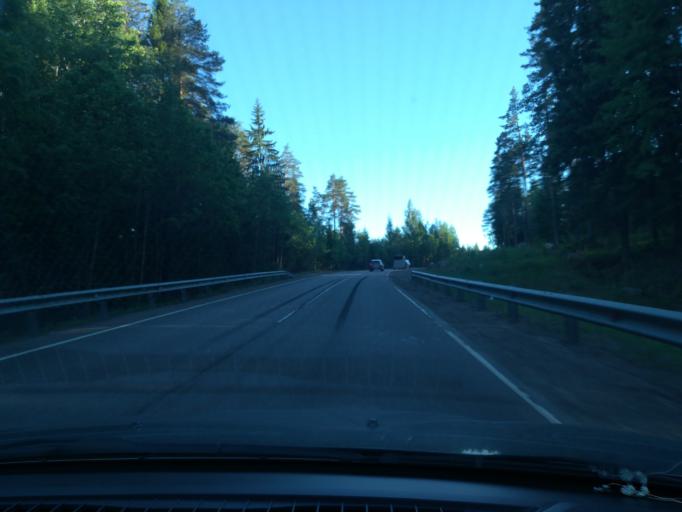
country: RU
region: Leningrad
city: Lesogorskiy
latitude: 60.9972
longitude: 28.9150
